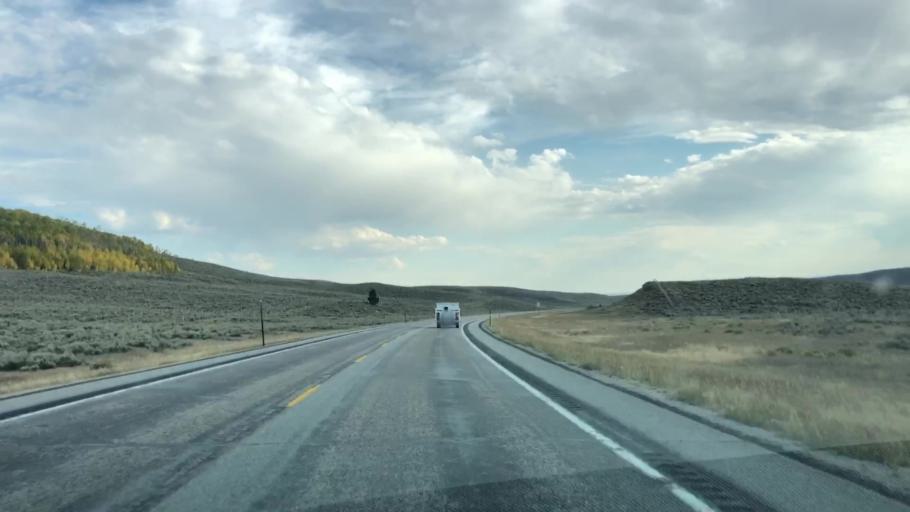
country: US
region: Wyoming
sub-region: Sublette County
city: Pinedale
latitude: 43.0852
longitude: -110.1628
